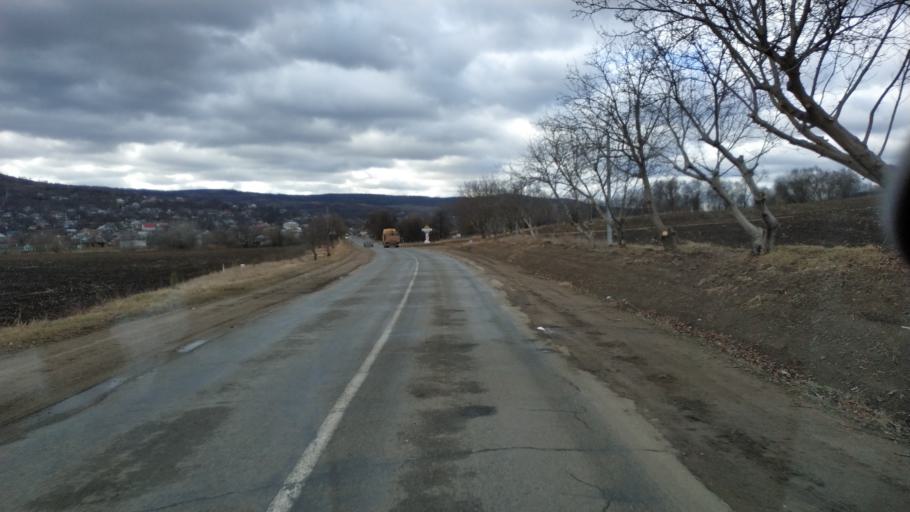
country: MD
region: Stinga Nistrului
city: Bucovat
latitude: 47.1657
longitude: 28.4367
